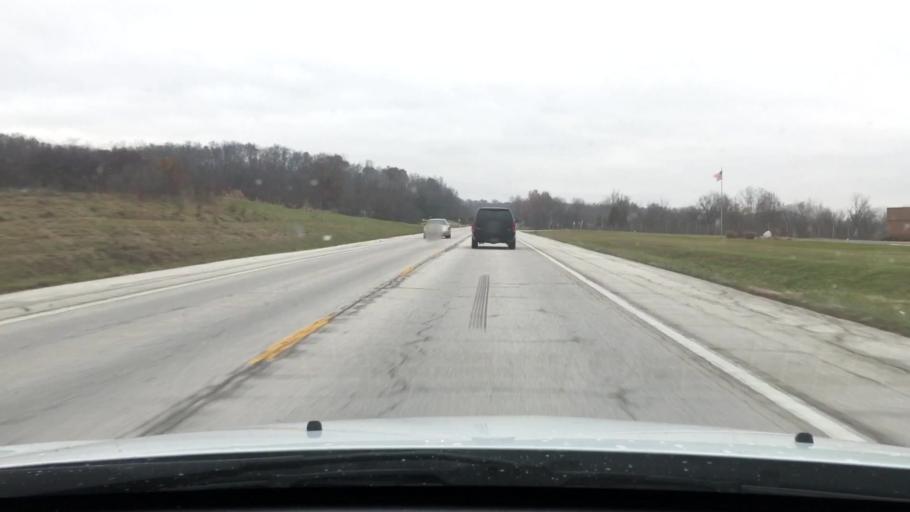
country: US
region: Missouri
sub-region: Pike County
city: Louisiana
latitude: 39.4273
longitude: -91.0836
